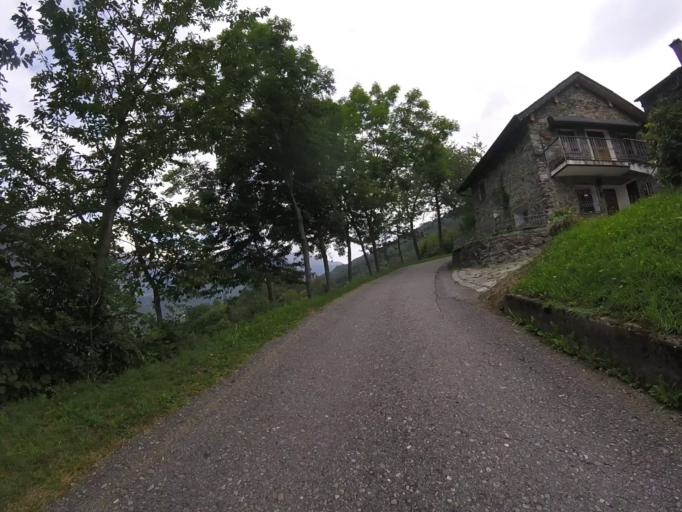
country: IT
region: Lombardy
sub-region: Provincia di Sondrio
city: Mazzo di Valtellina
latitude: 46.2632
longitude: 10.2698
